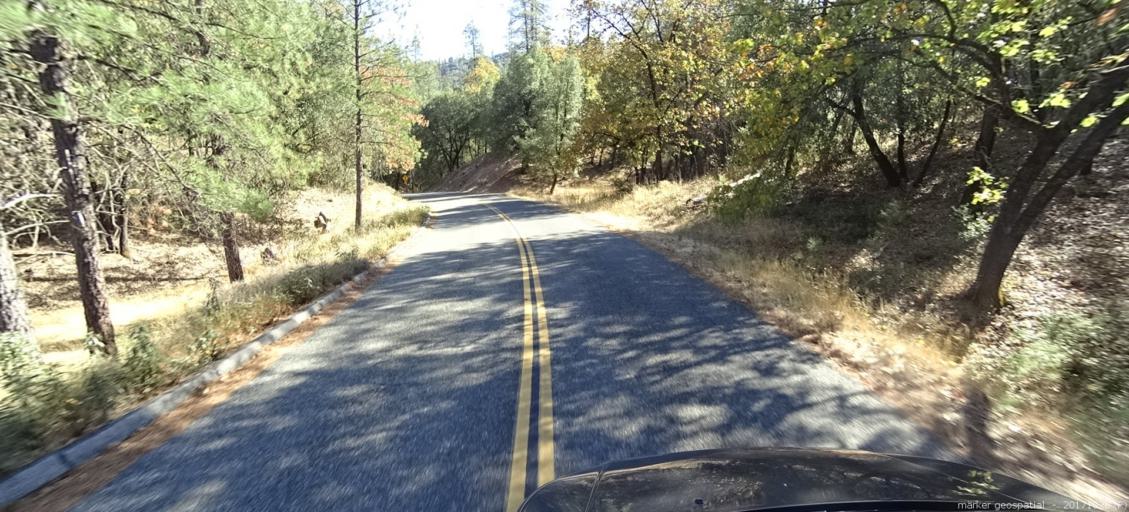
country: US
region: California
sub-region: Shasta County
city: Shasta
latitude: 40.6135
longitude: -122.5768
